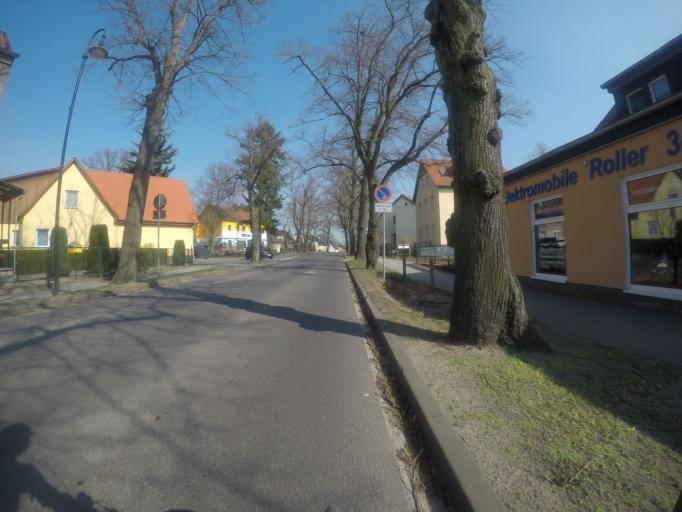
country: DE
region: Brandenburg
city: Konigs Wusterhausen
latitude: 52.2990
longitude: 13.6983
